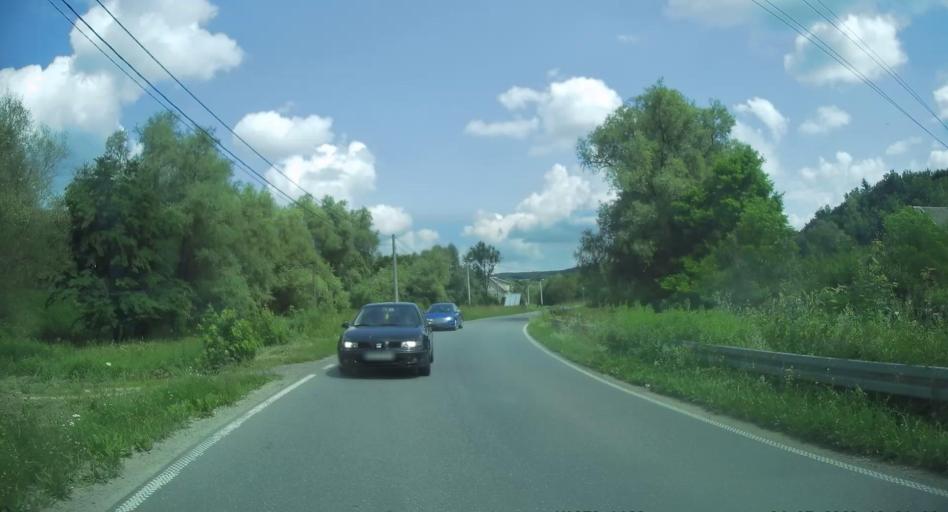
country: PL
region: Lesser Poland Voivodeship
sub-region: Powiat nowosadecki
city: Korzenna
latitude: 49.7420
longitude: 20.7681
